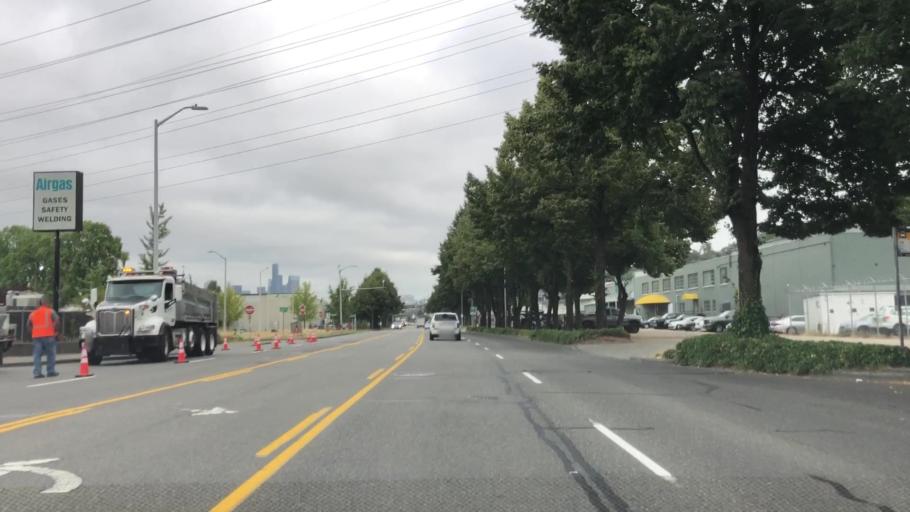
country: US
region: Washington
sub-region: King County
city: Seattle
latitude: 47.5640
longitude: -122.3228
